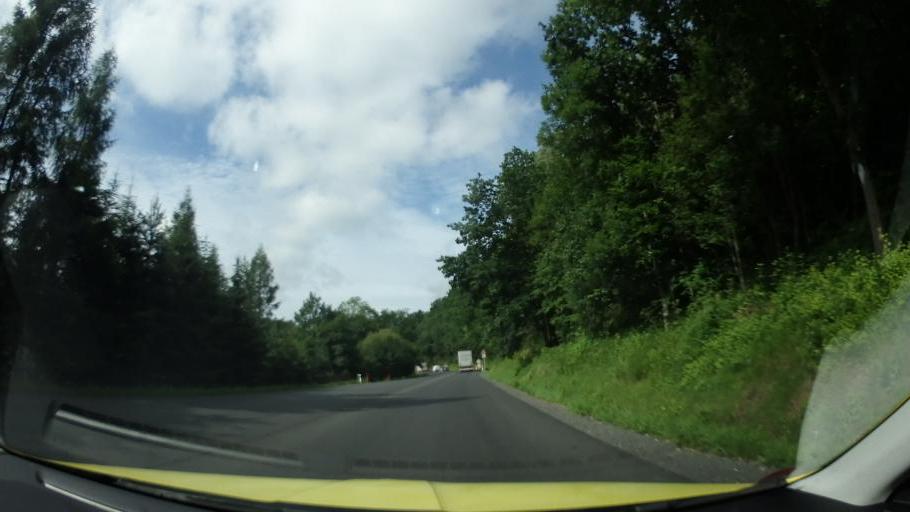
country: CZ
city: Hodslavice
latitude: 49.5598
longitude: 18.0251
